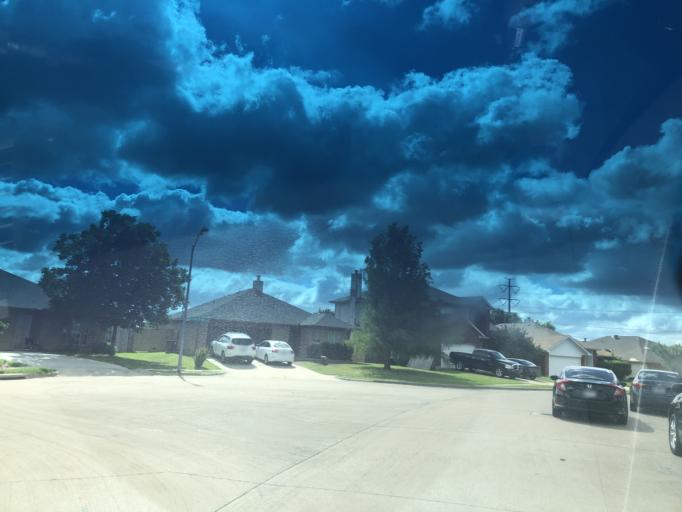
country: US
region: Texas
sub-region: Dallas County
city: Grand Prairie
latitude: 32.6996
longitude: -97.0302
